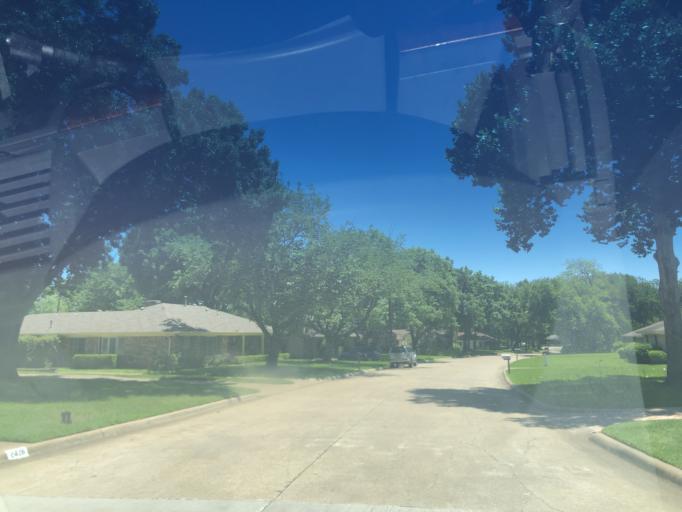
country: US
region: Texas
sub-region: Dallas County
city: Grand Prairie
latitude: 32.7732
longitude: -97.0388
